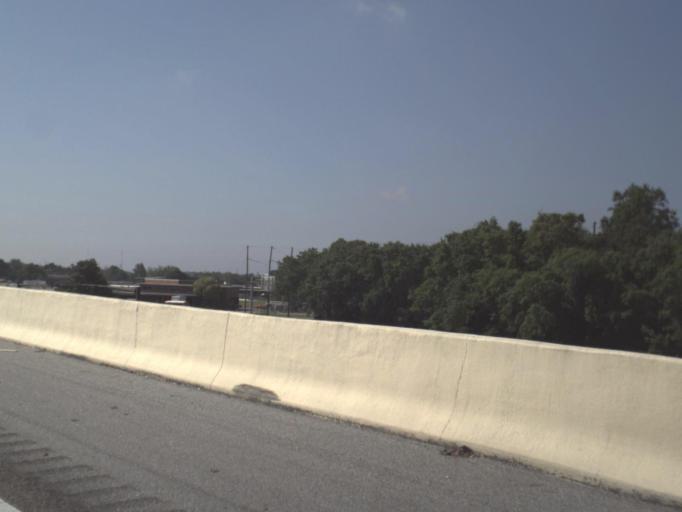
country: US
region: Florida
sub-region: Escambia County
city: Goulding
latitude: 30.4530
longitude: -87.2226
